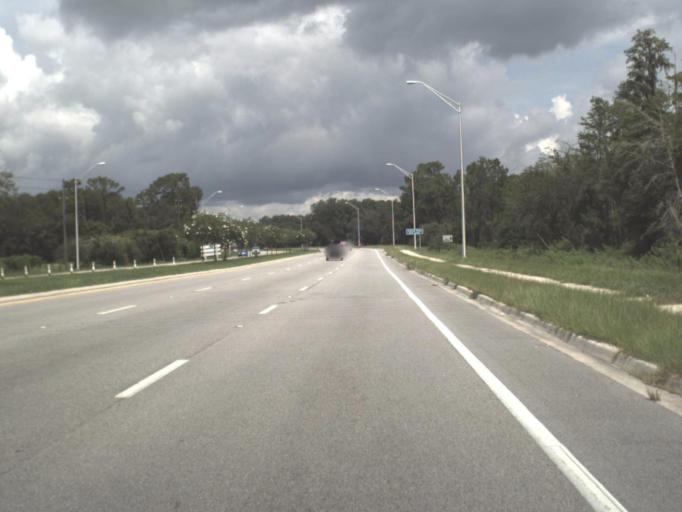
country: US
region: Florida
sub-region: Pasco County
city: Wesley Chapel
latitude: 28.2387
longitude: -82.3075
